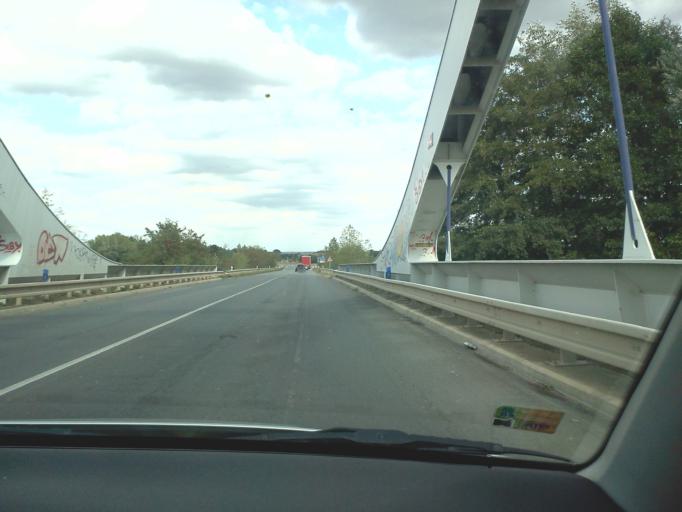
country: CZ
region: Central Bohemia
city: Lysa nad Labem
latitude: 50.1773
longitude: 14.8553
